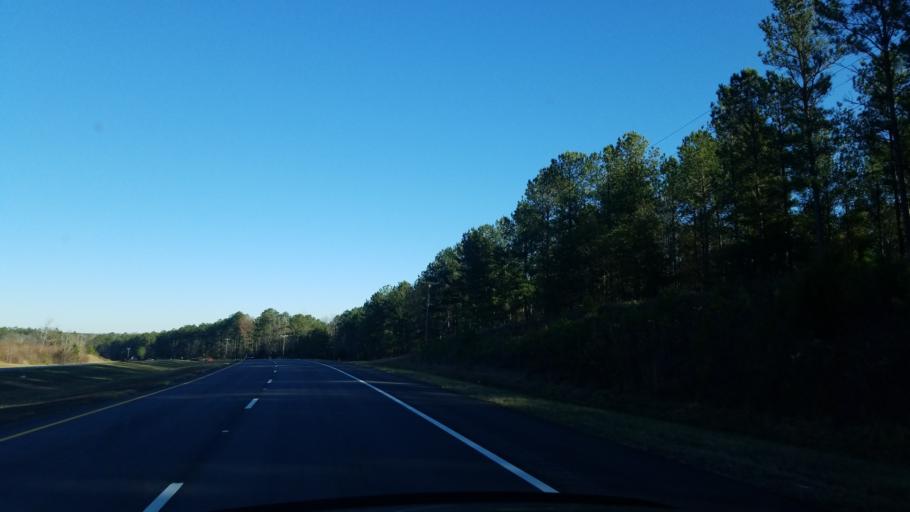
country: US
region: Georgia
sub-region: Talbot County
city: Talbotton
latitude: 32.5615
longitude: -84.6176
